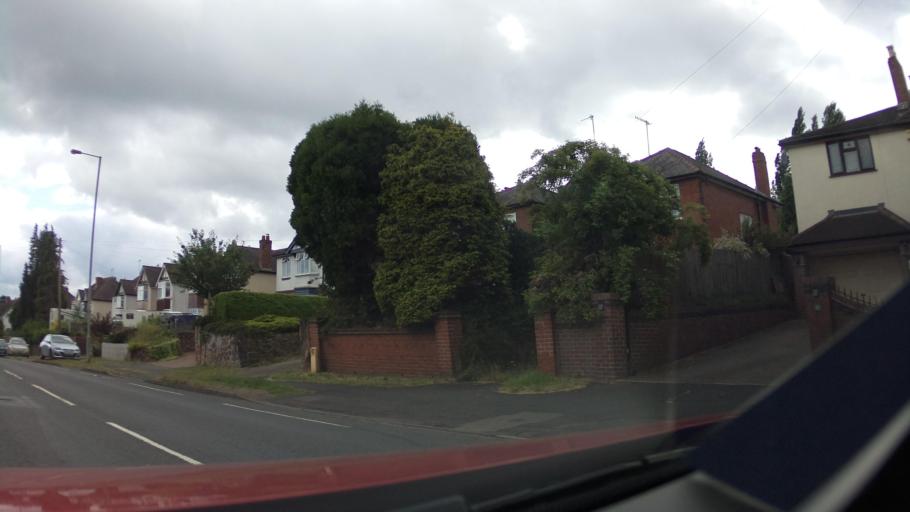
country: GB
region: England
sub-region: Worcestershire
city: Kidderminster
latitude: 52.3780
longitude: -2.2402
